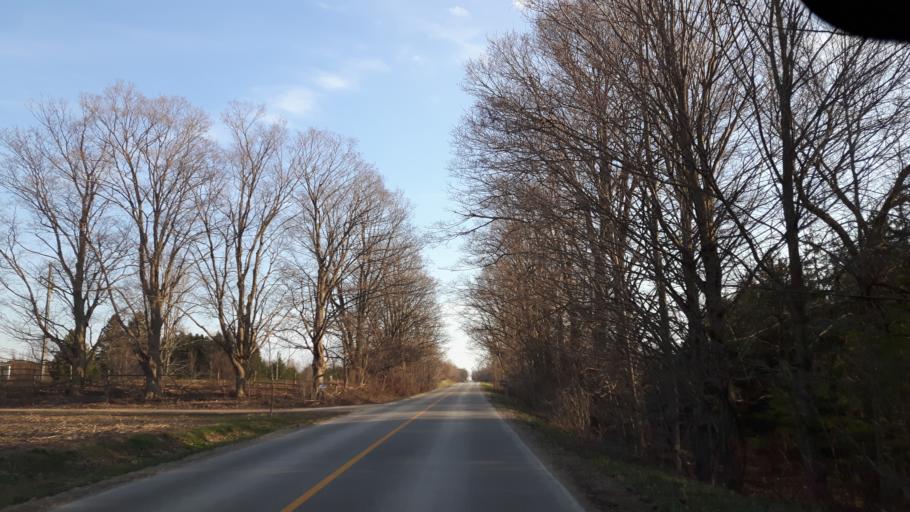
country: CA
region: Ontario
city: Goderich
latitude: 43.6793
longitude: -81.6644
